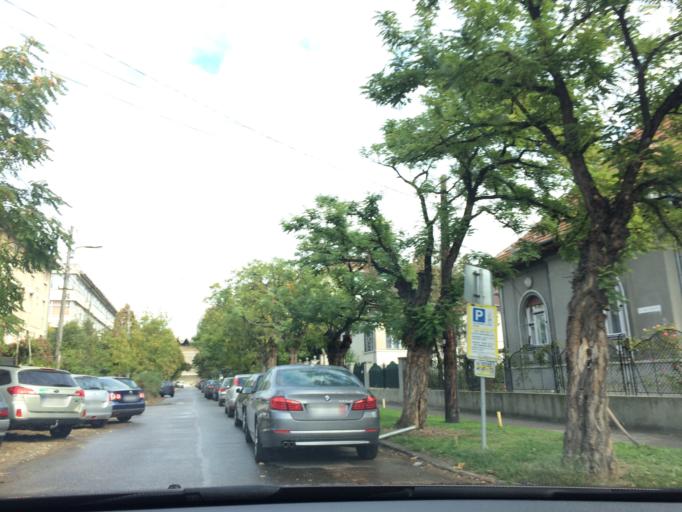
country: RO
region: Timis
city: Timisoara
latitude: 45.7448
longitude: 21.2321
